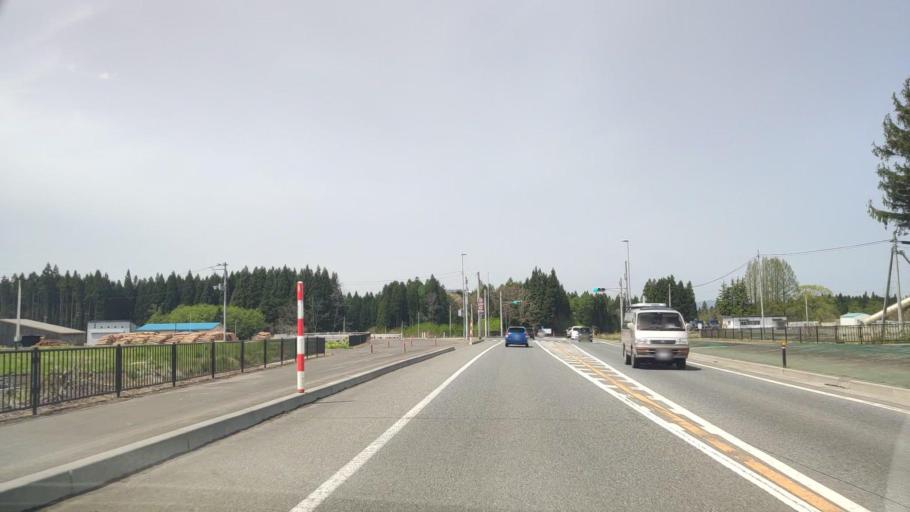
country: JP
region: Aomori
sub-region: Misawa Shi
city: Inuotose
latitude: 40.6771
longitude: 141.1740
